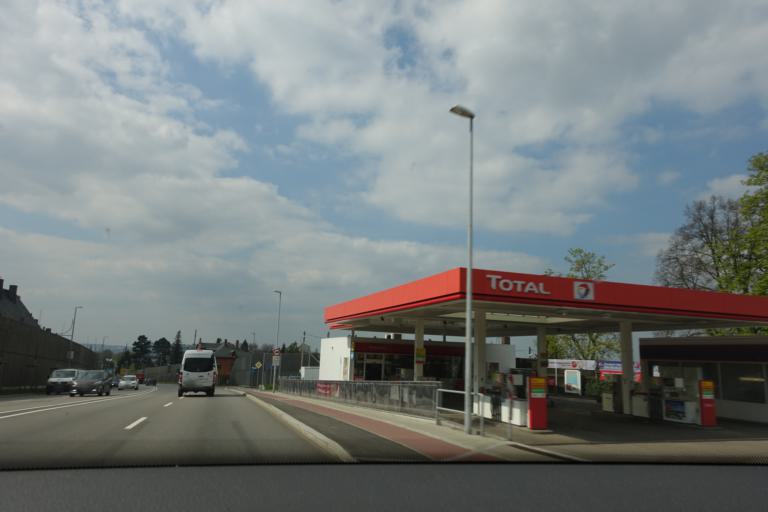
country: DE
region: Saxony
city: Chemnitz
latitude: 50.8098
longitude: 12.9654
